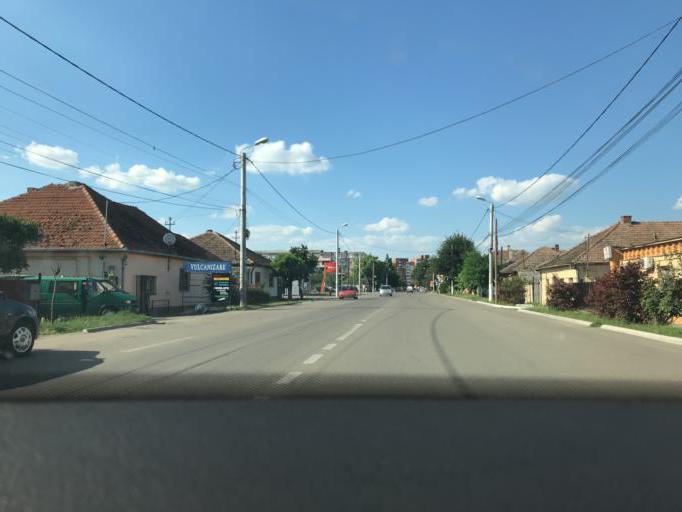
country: RO
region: Bihor
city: Margita
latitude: 47.3394
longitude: 22.3309
